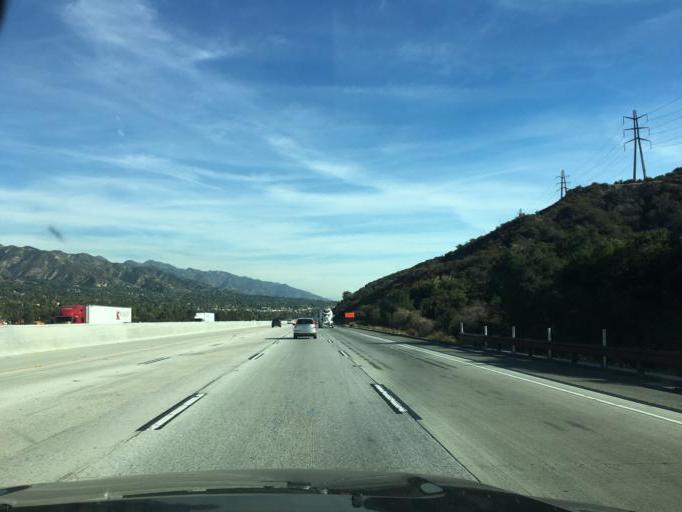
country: US
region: California
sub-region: Los Angeles County
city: La Crescenta-Montrose
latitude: 34.2333
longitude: -118.2760
